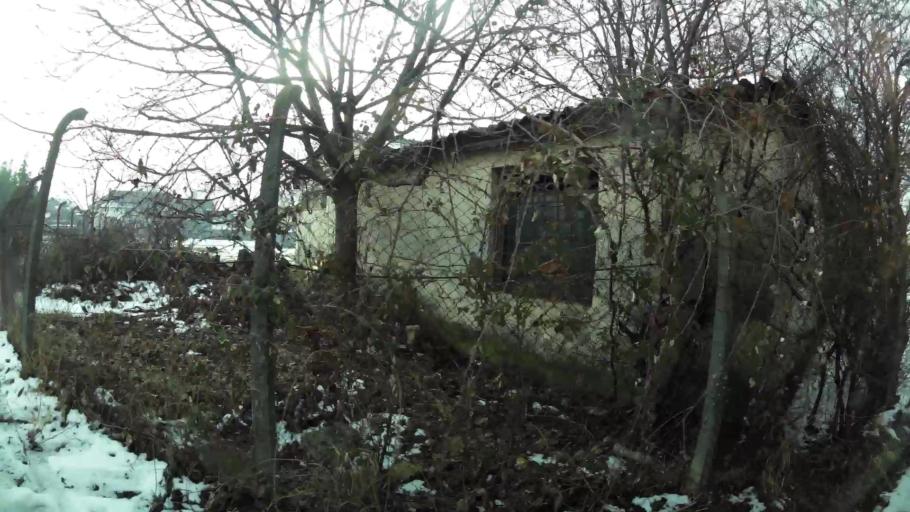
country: MK
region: Ilinden
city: Ilinden
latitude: 41.9932
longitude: 21.5826
